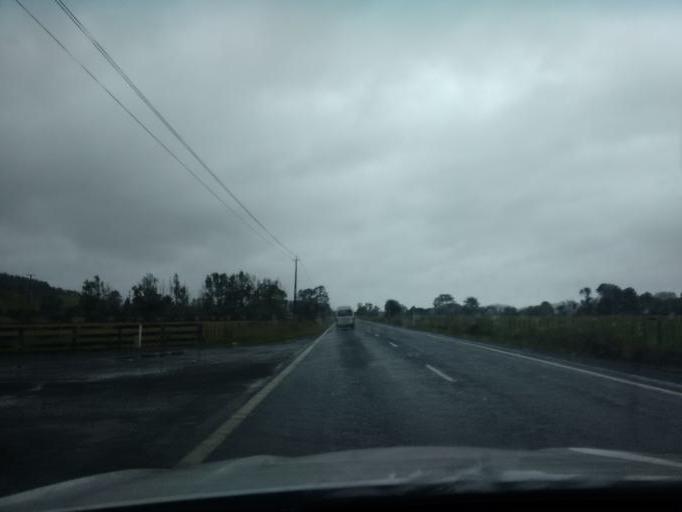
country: NZ
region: Waikato
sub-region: Thames-Coromandel District
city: Whitianga
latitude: -36.8559
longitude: 175.6518
